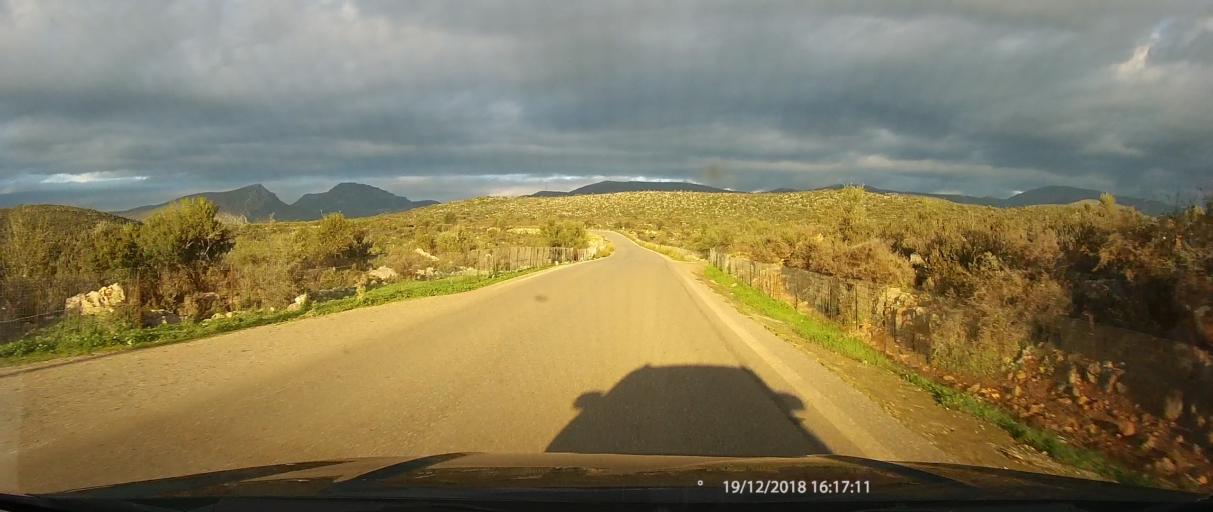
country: GR
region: Peloponnese
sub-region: Nomos Lakonias
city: Kato Glikovrisi
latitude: 36.9079
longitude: 22.8088
